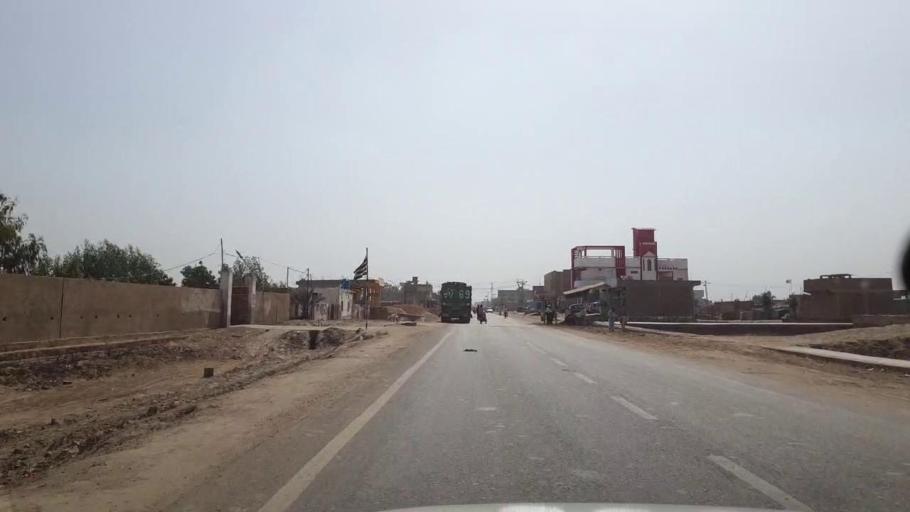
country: PK
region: Sindh
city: Matli
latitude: 25.0549
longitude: 68.6435
